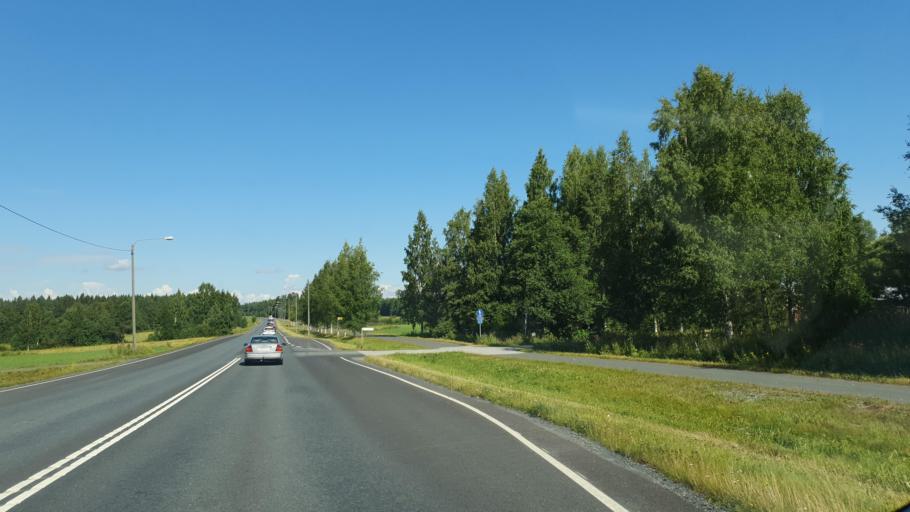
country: FI
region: Northern Savo
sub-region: Ylae-Savo
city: Lapinlahti
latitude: 63.4331
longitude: 27.3270
